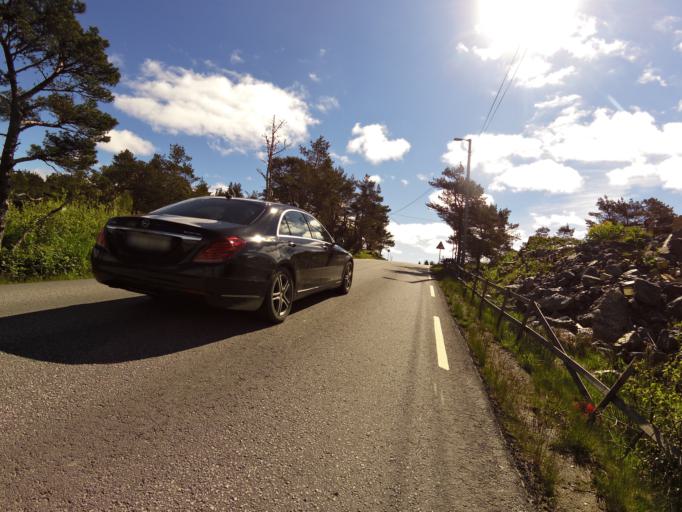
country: NO
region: Hordaland
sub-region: Os
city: Hagavik
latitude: 60.2572
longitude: 5.3612
